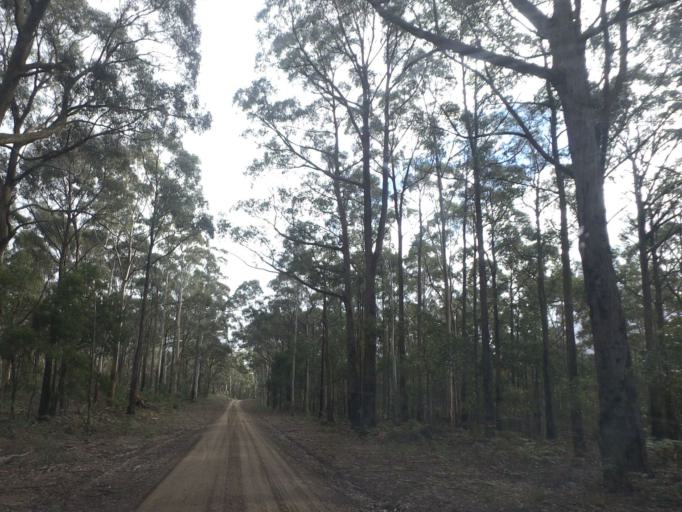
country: AU
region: Victoria
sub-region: Moorabool
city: Bacchus Marsh
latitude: -37.4452
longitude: 144.3248
